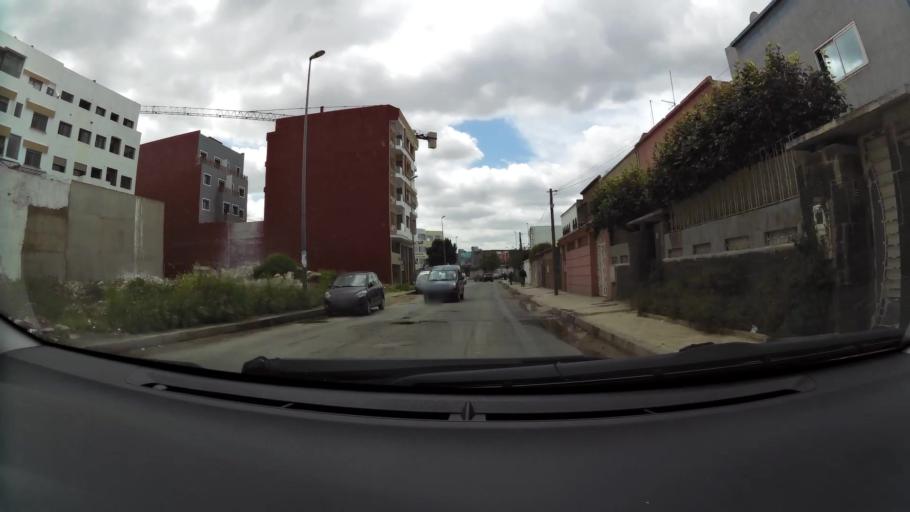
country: MA
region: Grand Casablanca
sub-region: Casablanca
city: Casablanca
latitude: 33.6060
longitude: -7.5485
